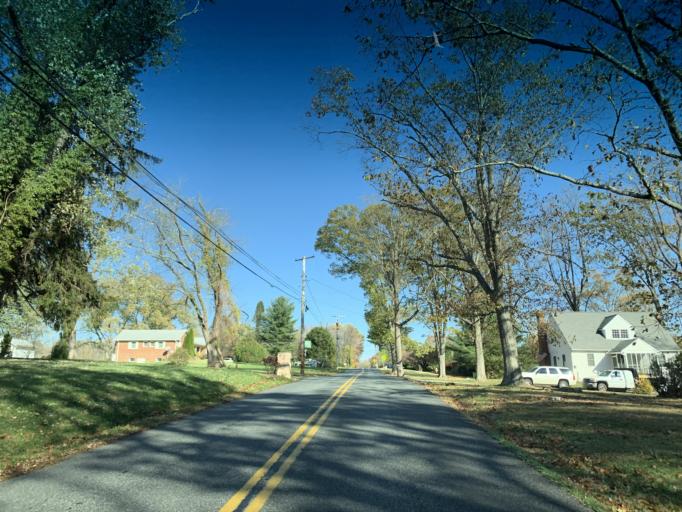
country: US
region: Maryland
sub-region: Harford County
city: Joppatowne
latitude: 39.4780
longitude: -76.3530
